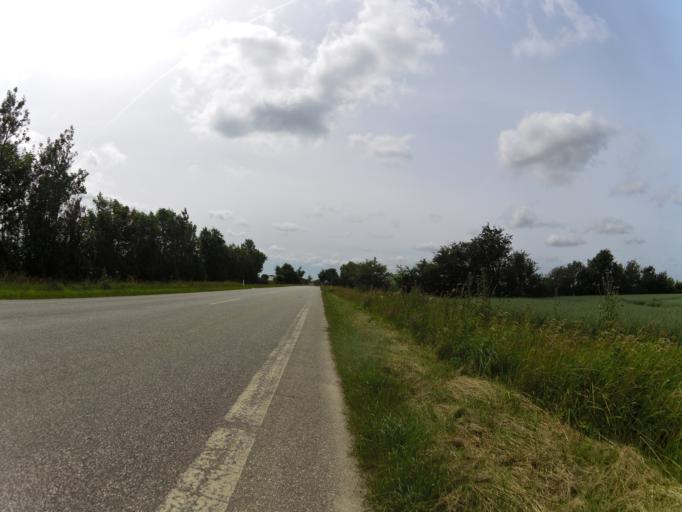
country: DK
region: North Denmark
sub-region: Bronderslev Kommune
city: Dronninglund
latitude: 57.2711
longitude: 10.3486
